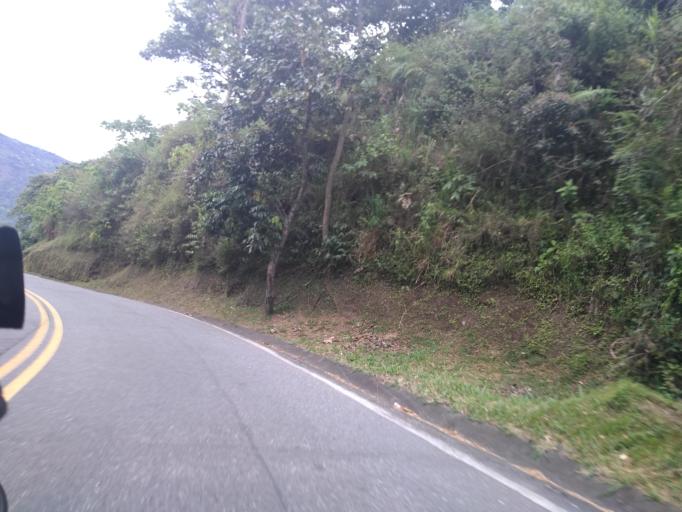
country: CO
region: Cauca
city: Rosas
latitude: 2.2421
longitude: -76.7692
